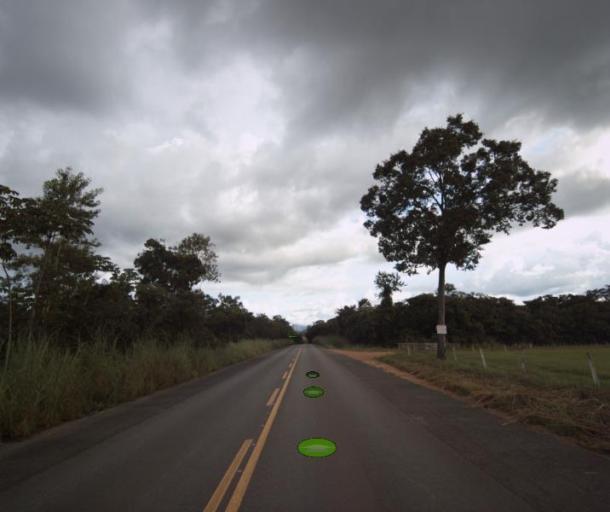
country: BR
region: Goias
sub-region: Niquelandia
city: Niquelandia
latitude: -14.5088
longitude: -48.5194
